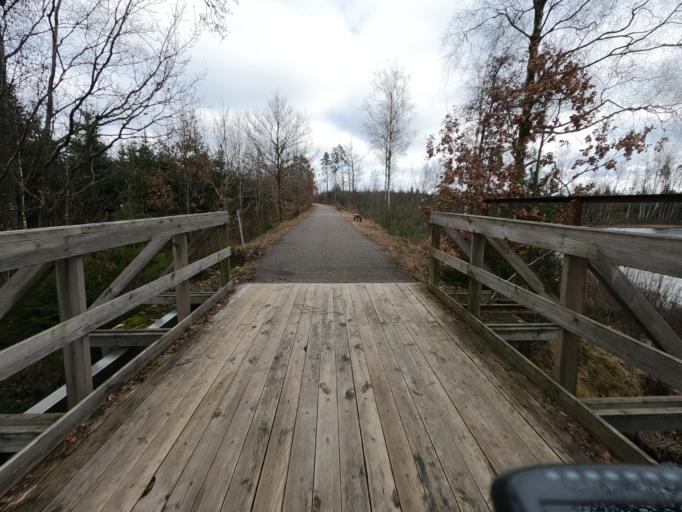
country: SE
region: Joenkoeping
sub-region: Varnamo Kommun
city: Rydaholm
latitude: 56.8424
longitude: 14.2263
